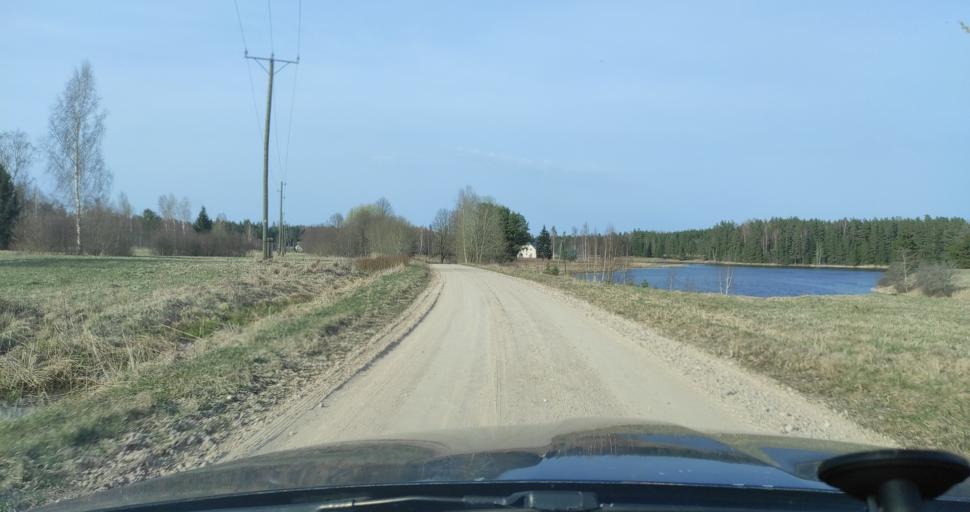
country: LV
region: Kuldigas Rajons
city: Kuldiga
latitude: 57.0062
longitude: 22.0144
